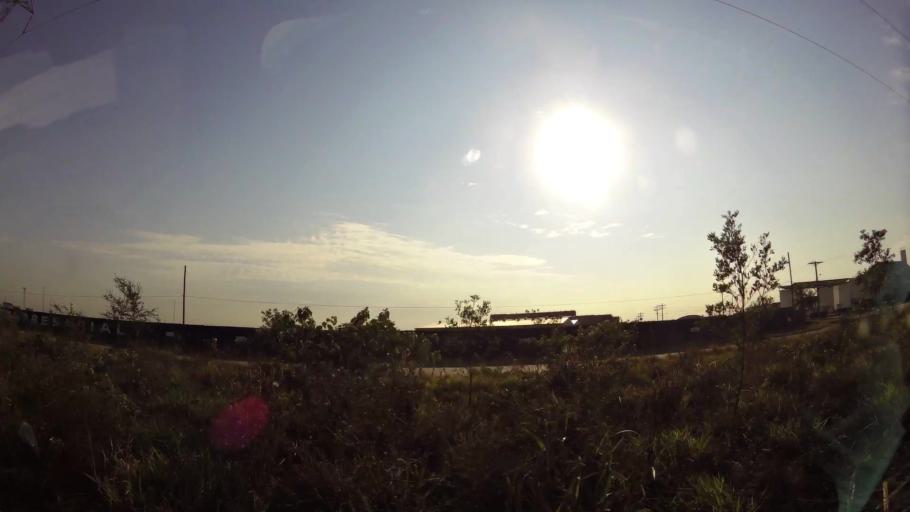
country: BO
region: Santa Cruz
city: Santa Cruz de la Sierra
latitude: -17.6763
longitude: -63.1570
